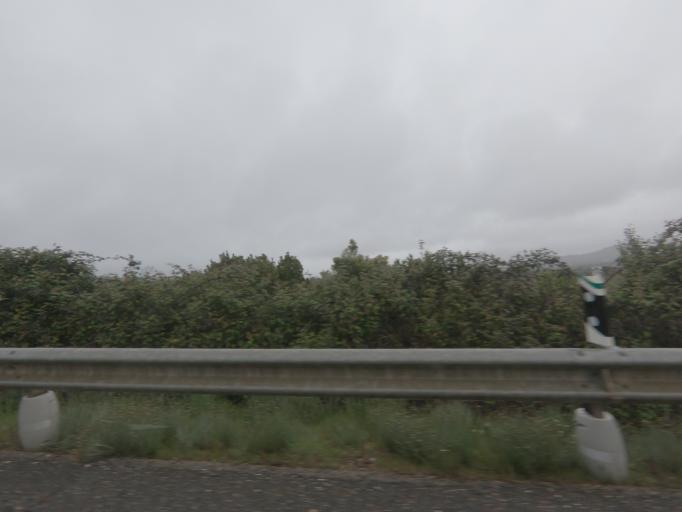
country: ES
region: Extremadura
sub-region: Provincia de Badajoz
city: Puebla de Obando
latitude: 39.1686
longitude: -6.6302
